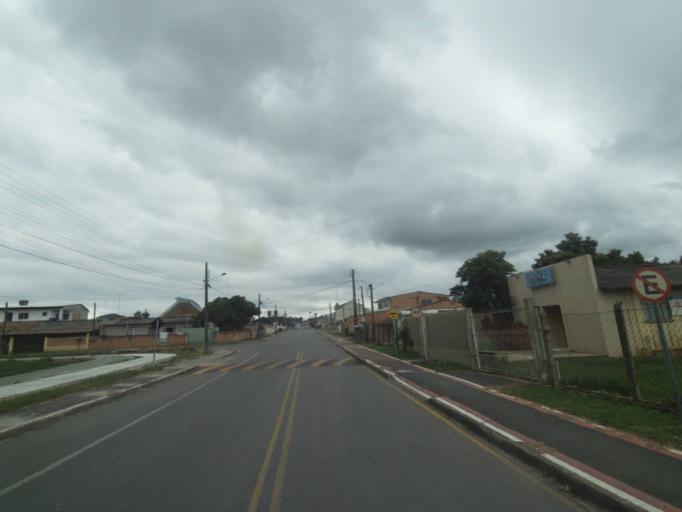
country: BR
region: Parana
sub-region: Quatro Barras
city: Quatro Barras
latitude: -25.3560
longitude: -49.1062
